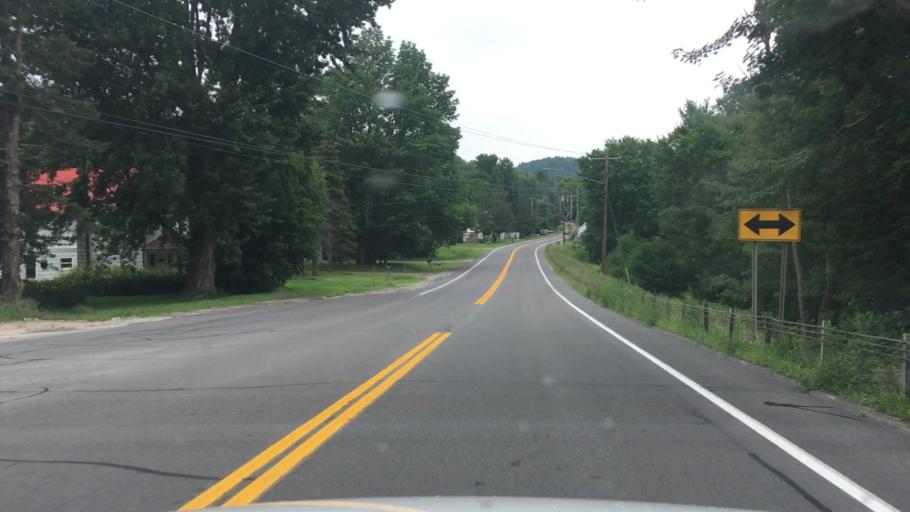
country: US
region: New York
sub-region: Essex County
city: Keeseville
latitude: 44.4653
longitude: -73.5871
